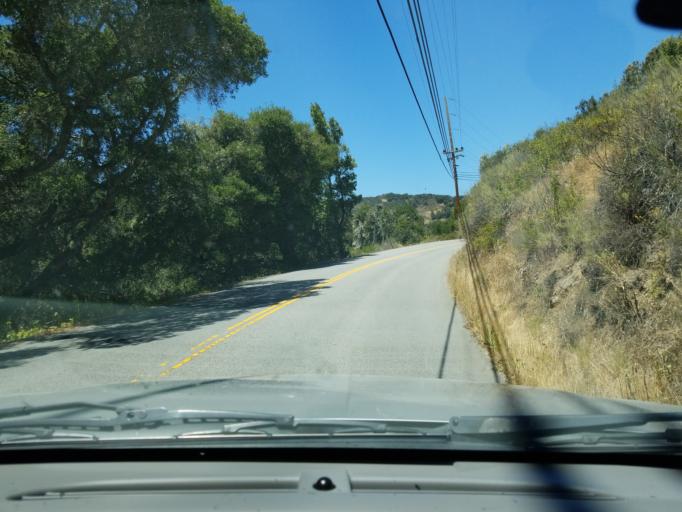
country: US
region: California
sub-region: Monterey County
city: Carmel Valley Village
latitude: 36.4615
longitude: -121.7100
